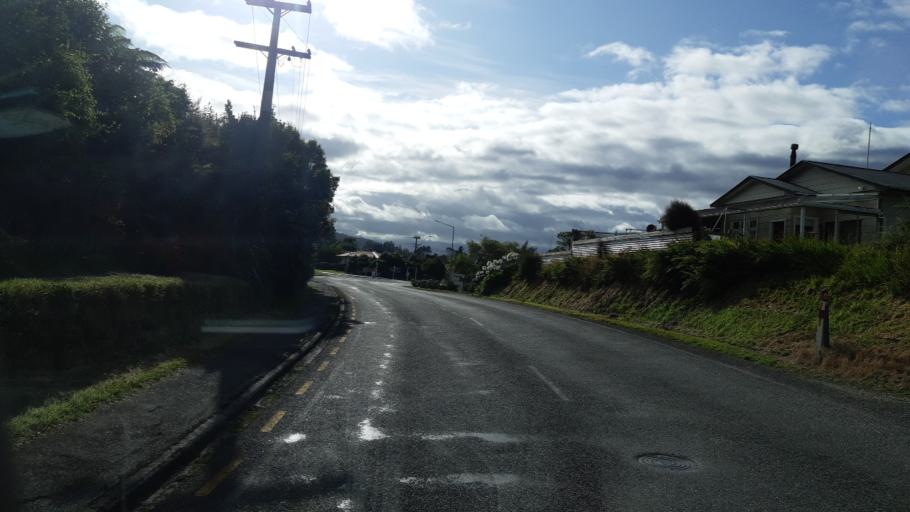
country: NZ
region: West Coast
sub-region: Westland District
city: Hokitika
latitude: -42.7477
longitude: 171.0057
